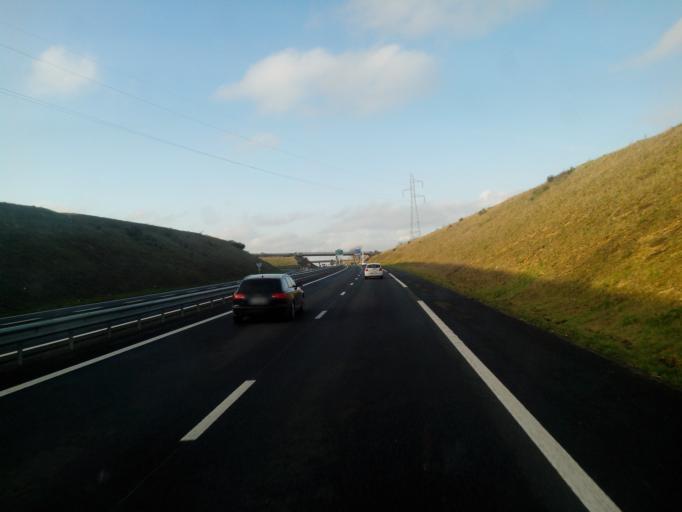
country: FR
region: Pays de la Loire
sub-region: Departement de Maine-et-Loire
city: La Tessoualle
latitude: 47.0199
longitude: -0.8782
